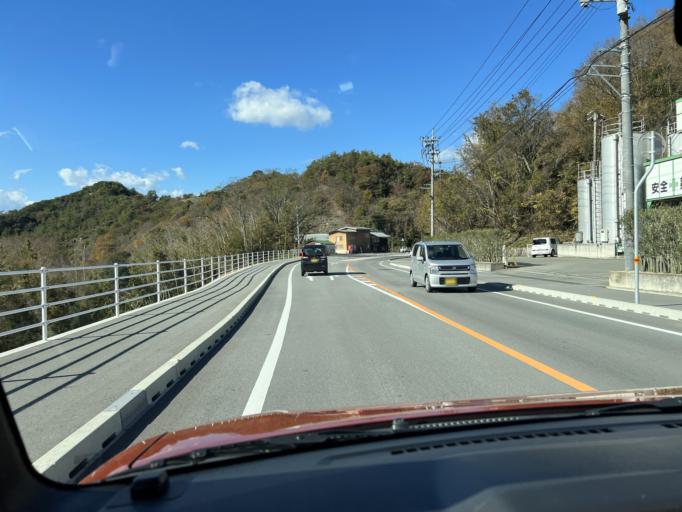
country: JP
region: Kagawa
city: Tonosho
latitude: 34.4760
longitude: 134.2509
